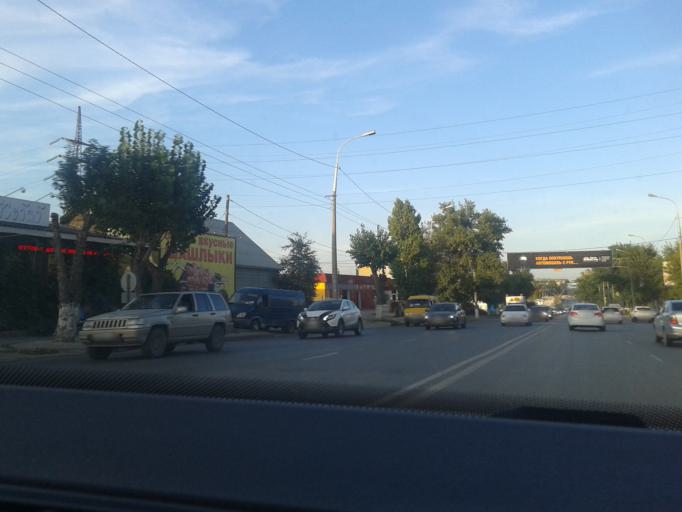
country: RU
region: Volgograd
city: Volgograd
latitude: 48.7048
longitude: 44.4830
